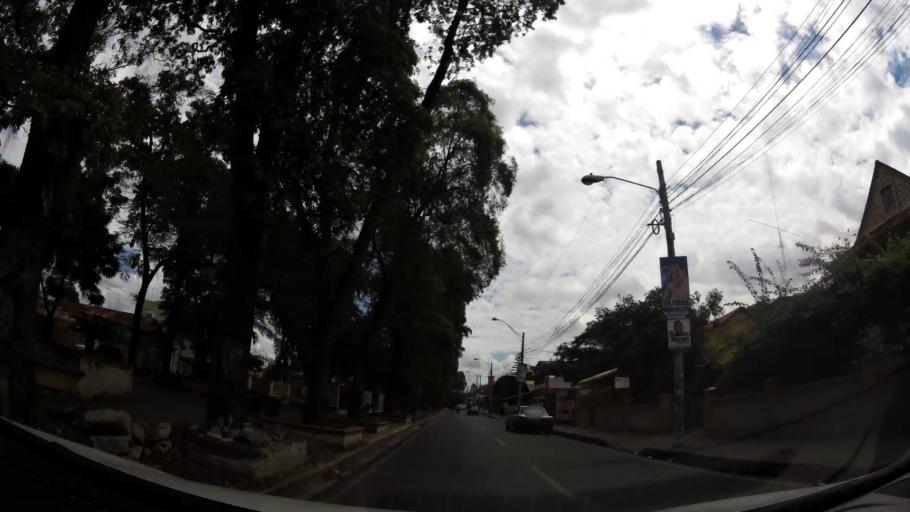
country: DO
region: Santiago
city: Santiago de los Caballeros
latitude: 19.4562
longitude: -70.7111
